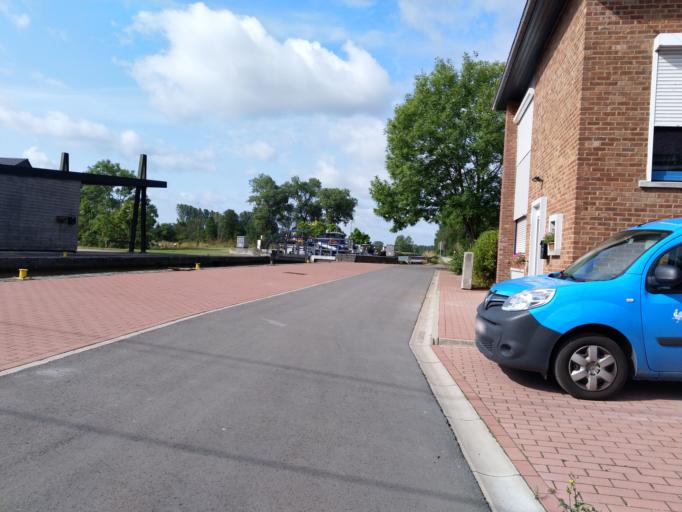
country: BE
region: Wallonia
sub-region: Province du Hainaut
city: Beloeil
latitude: 50.5699
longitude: 3.7694
